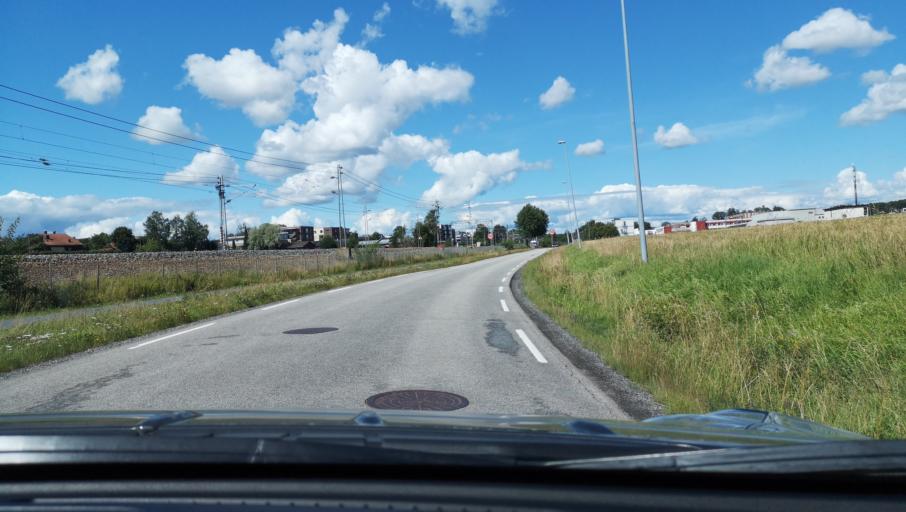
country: NO
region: Akershus
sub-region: As
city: As
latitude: 59.6585
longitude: 10.7976
